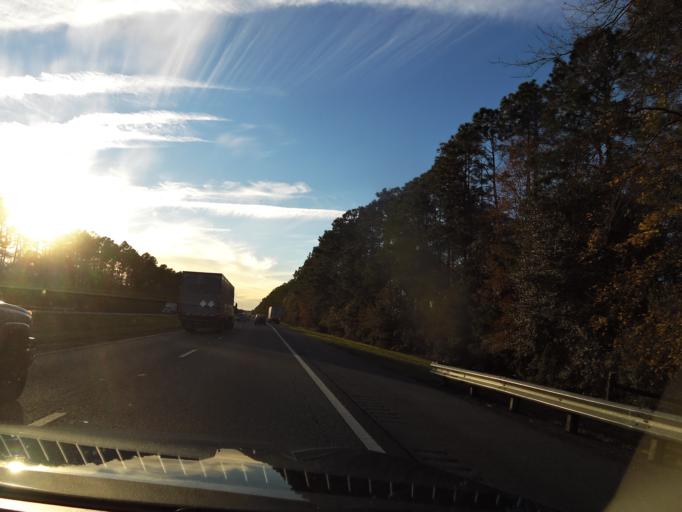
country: US
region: Florida
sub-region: Duval County
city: Baldwin
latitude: 30.2859
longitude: -82.0247
